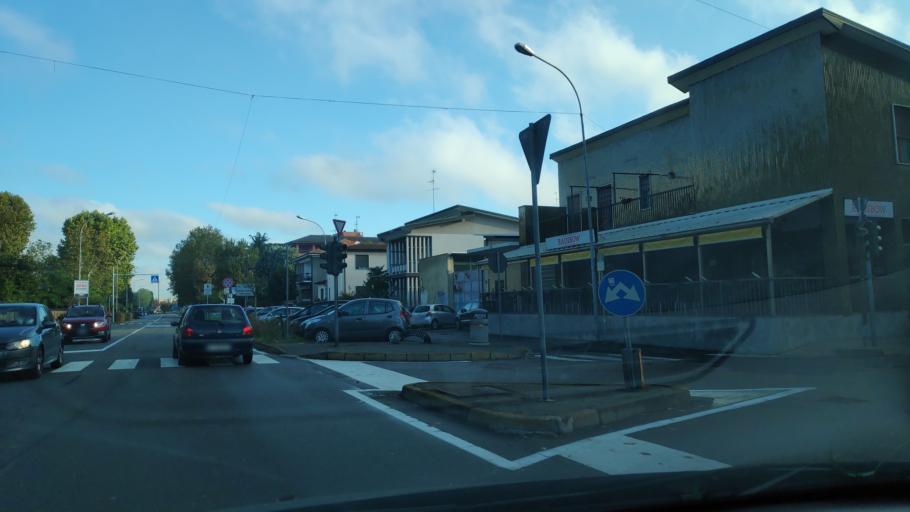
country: IT
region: Lombardy
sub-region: Citta metropolitana di Milano
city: Opera
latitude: 45.3772
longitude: 9.2124
